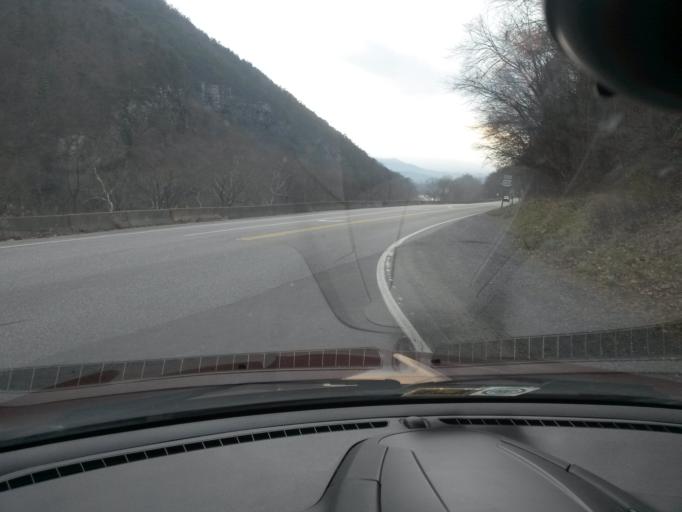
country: US
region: Virginia
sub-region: Alleghany County
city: Clifton Forge
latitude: 37.8127
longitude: -79.7991
